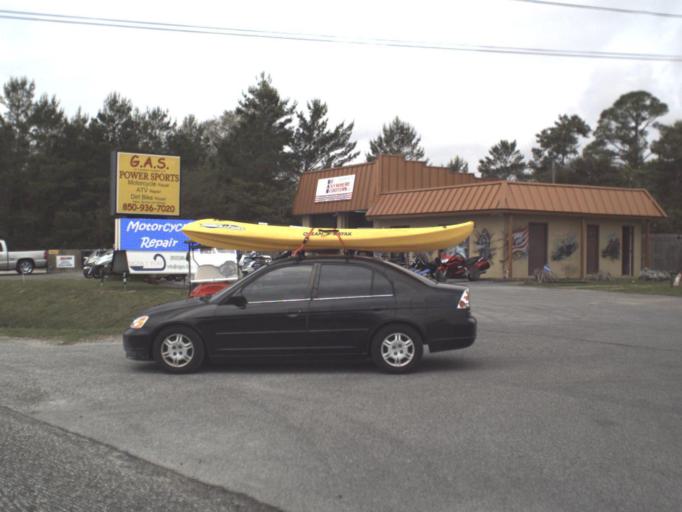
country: US
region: Florida
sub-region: Santa Rosa County
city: Navarre
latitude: 30.4086
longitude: -86.8437
